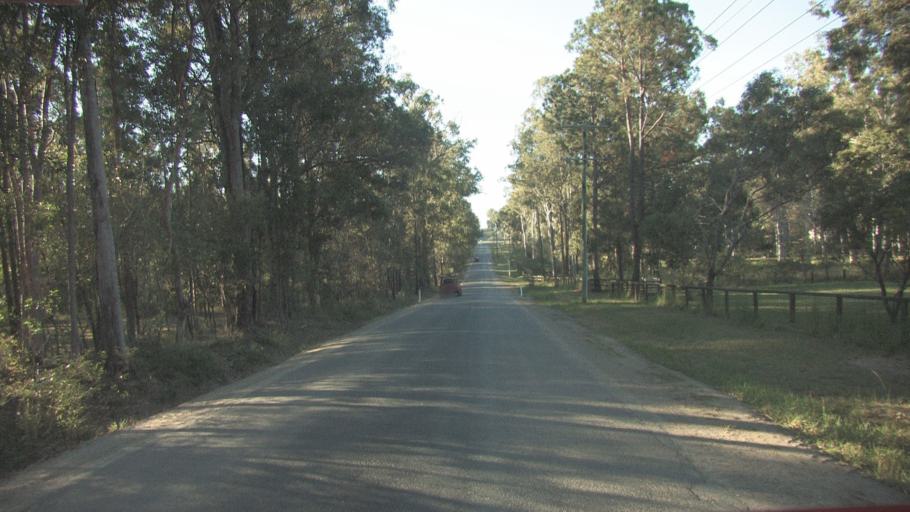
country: AU
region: Queensland
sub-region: Logan
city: Chambers Flat
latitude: -27.7740
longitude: 153.1368
